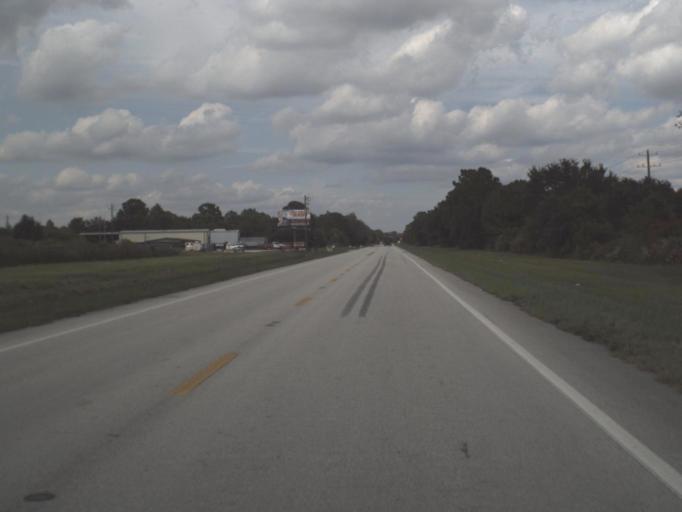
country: US
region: Florida
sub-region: Okeechobee County
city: Cypress Quarters
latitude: 27.3421
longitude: -80.8224
